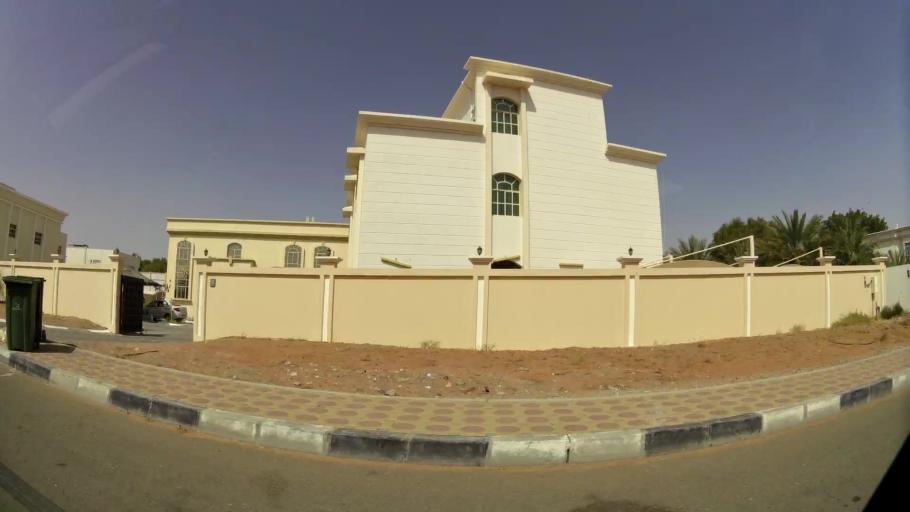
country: AE
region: Abu Dhabi
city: Al Ain
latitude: 24.2282
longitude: 55.6812
